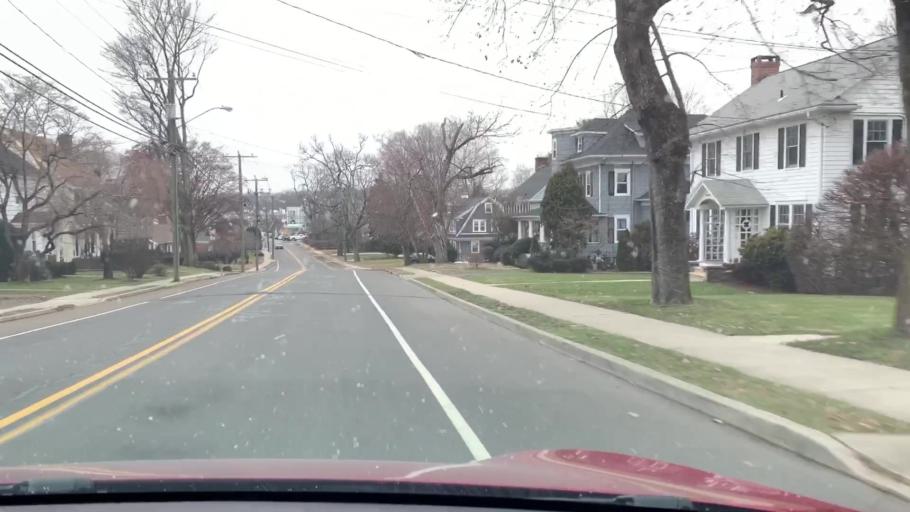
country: US
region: Connecticut
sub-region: Fairfield County
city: Stamford
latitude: 41.0669
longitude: -73.5398
